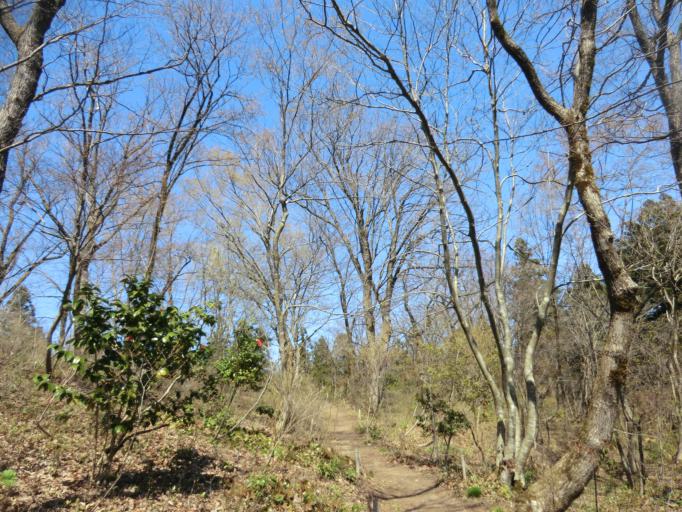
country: JP
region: Niigata
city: Nagaoka
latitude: 37.4624
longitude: 138.7471
